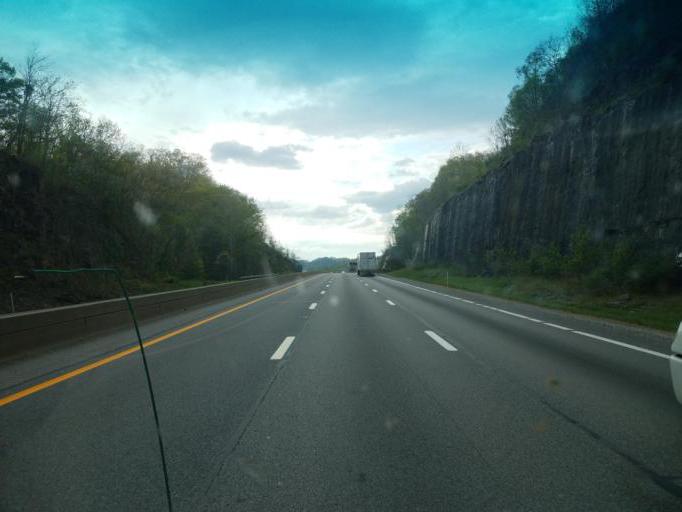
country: US
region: West Virginia
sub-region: Fayette County
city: Oak Hill
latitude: 37.9908
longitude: -81.3211
